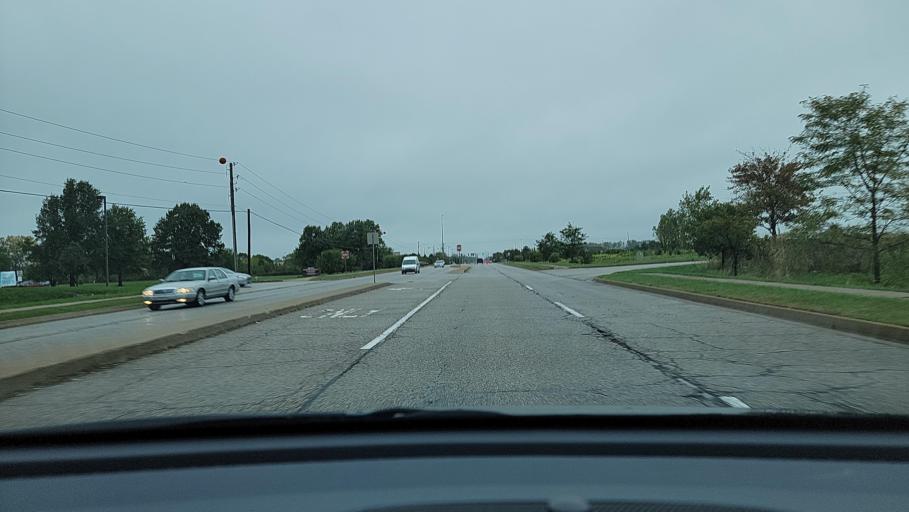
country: US
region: Indiana
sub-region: Porter County
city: Portage
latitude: 41.5468
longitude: -87.1825
